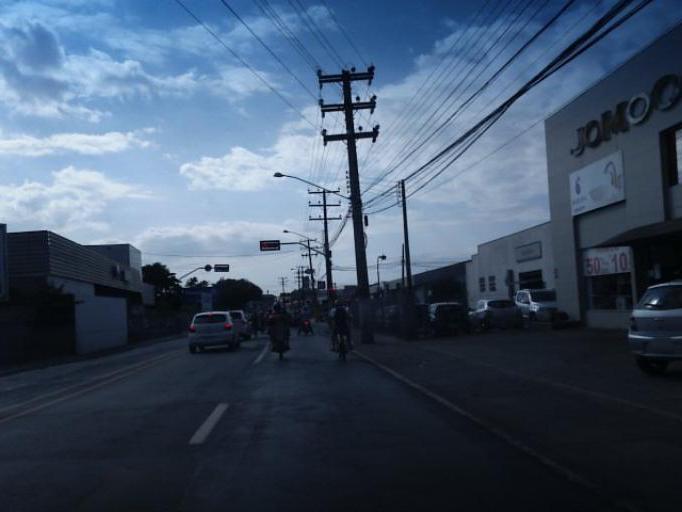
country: BR
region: Santa Catarina
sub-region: Itajai
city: Itajai
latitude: -26.8904
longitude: -48.6833
